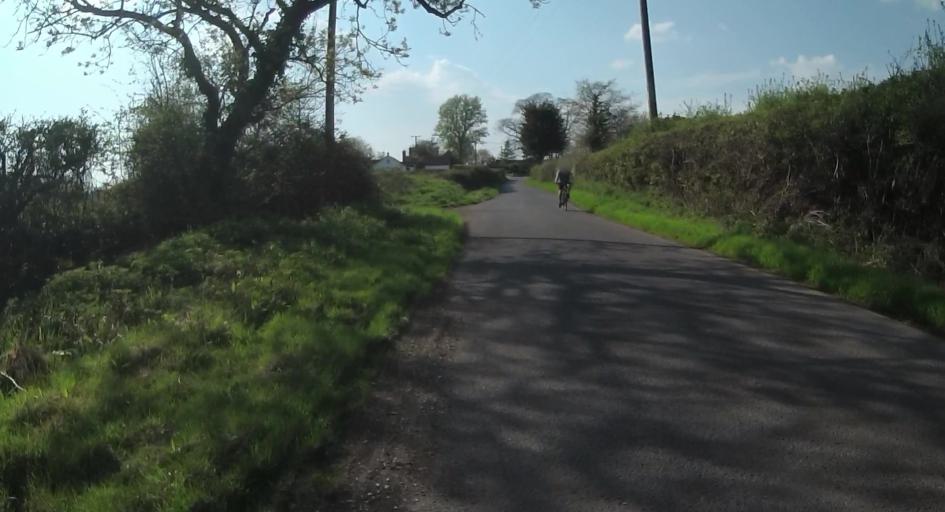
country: GB
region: England
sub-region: West Berkshire
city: Stratfield Mortimer
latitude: 51.3567
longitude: -1.0741
